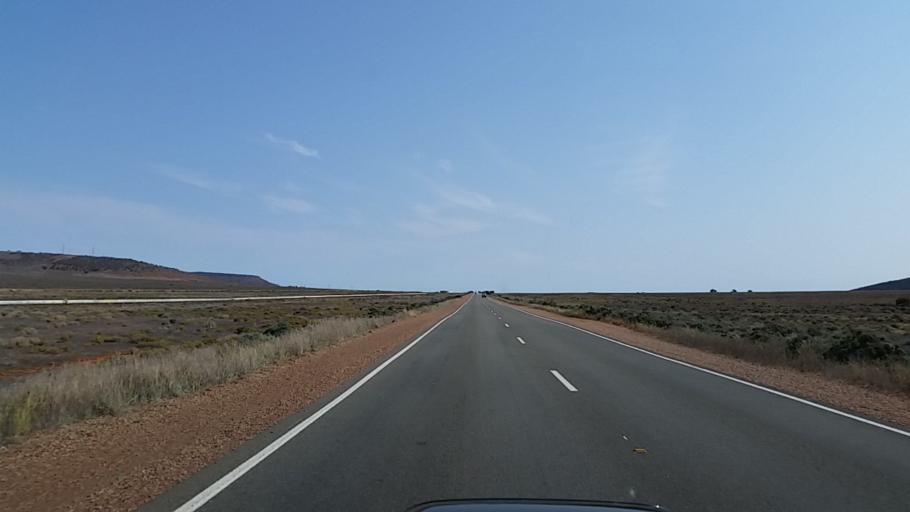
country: AU
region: South Australia
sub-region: Port Augusta
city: Port Augusta West
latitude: -32.5975
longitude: 137.5992
